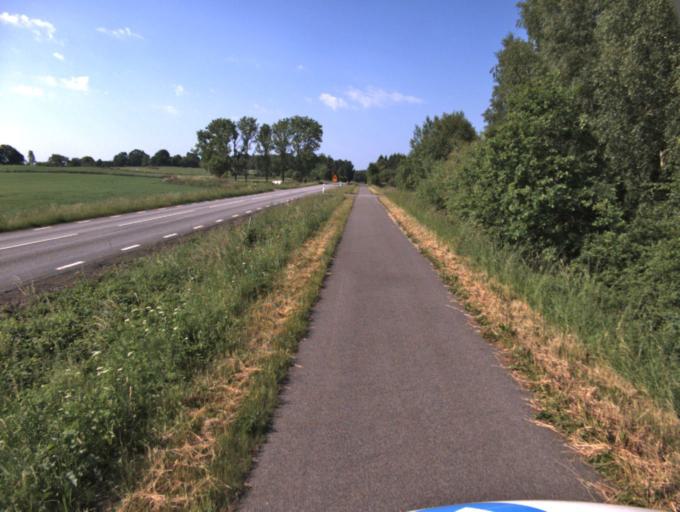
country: SE
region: Skane
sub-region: Kristianstads Kommun
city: Tollarp
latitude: 56.1647
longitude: 14.2783
